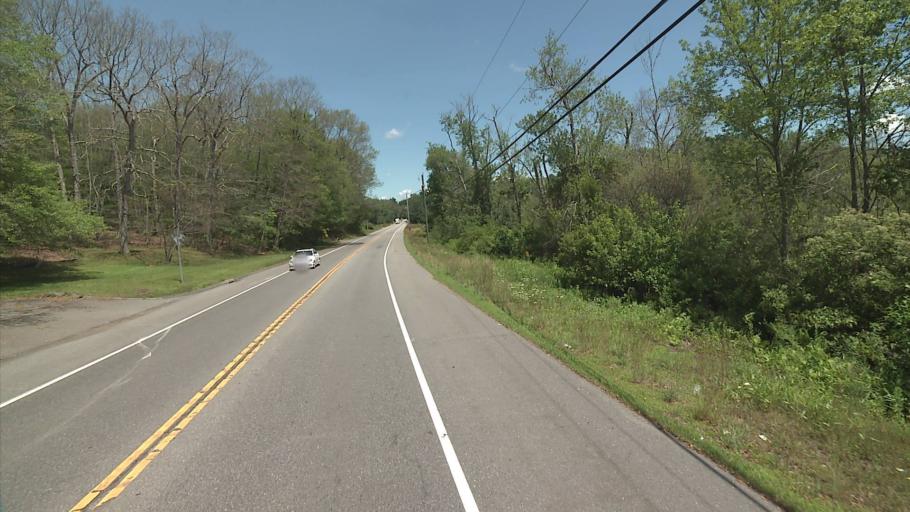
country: US
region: Connecticut
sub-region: New London County
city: Old Mystic
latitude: 41.4583
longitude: -71.9083
